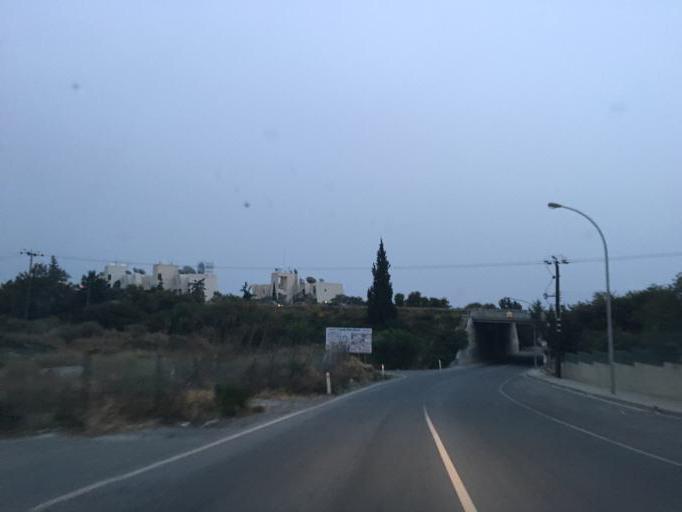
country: CY
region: Larnaka
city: Agios Tychon
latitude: 34.7167
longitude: 33.1635
